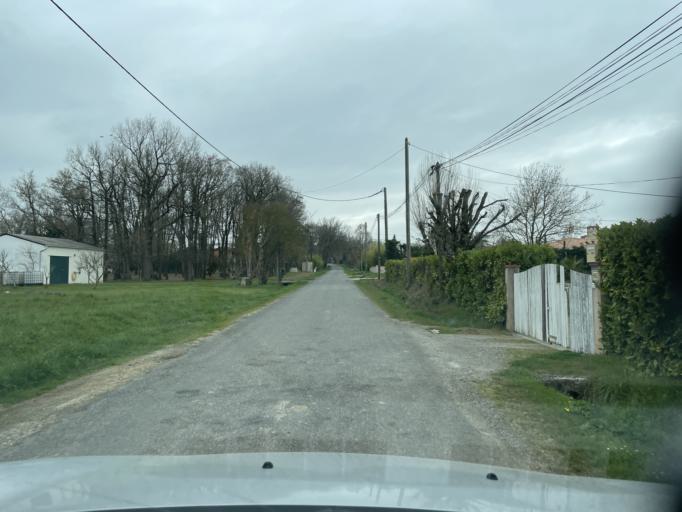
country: FR
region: Midi-Pyrenees
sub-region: Departement du Gers
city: Pujaudran
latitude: 43.6099
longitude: 1.1631
